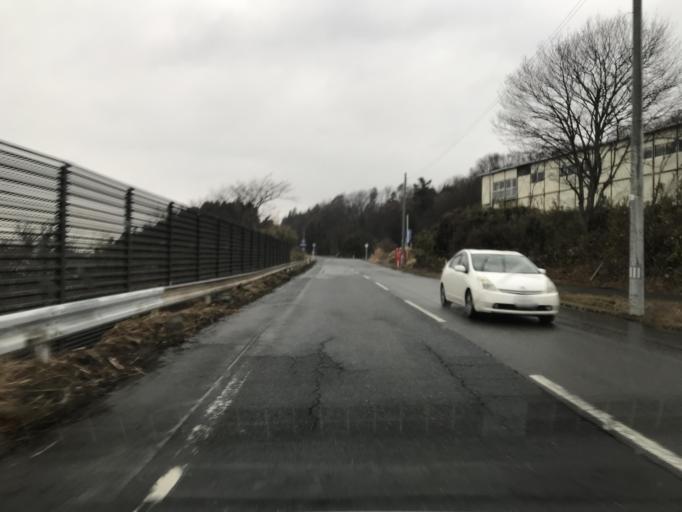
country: JP
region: Miyagi
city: Furukawa
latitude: 38.6785
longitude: 140.8729
